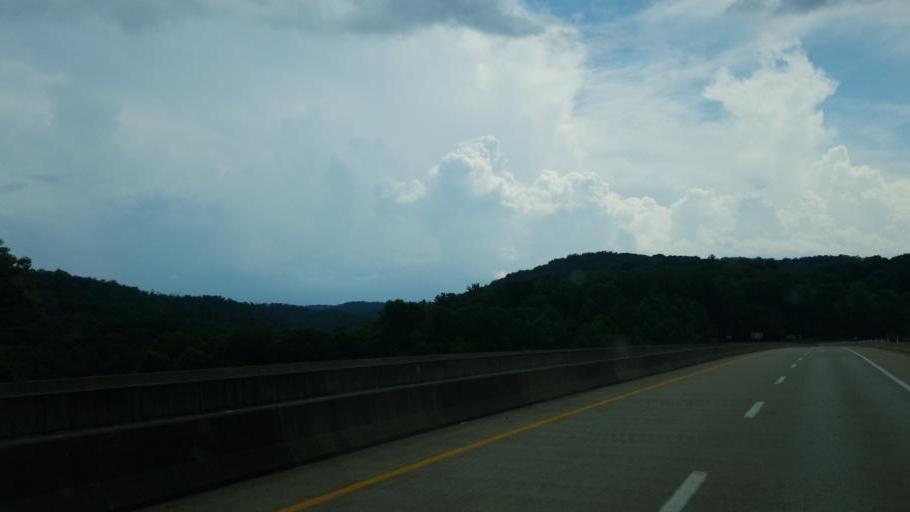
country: US
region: West Virginia
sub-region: Kanawha County
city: Alum Creek
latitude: 38.2688
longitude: -81.7882
